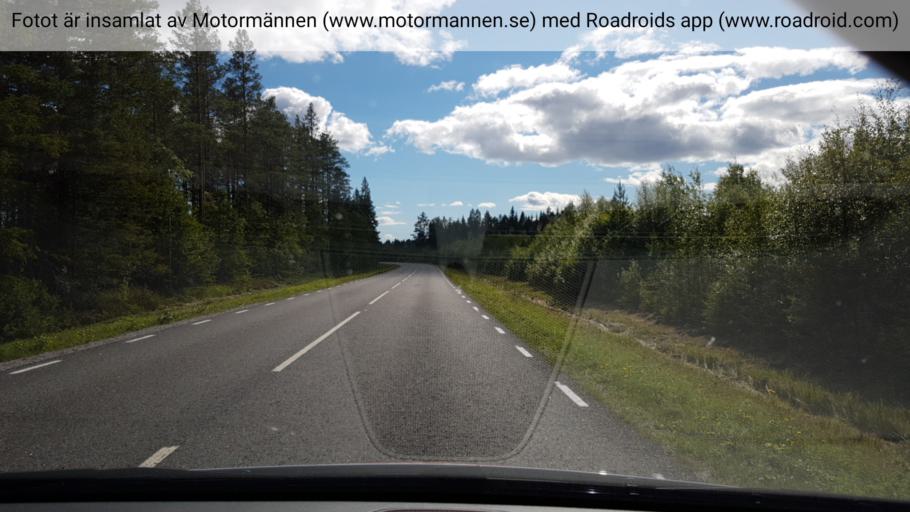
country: SE
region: Vaesterbotten
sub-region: Umea Kommun
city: Hoernefors
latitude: 63.6598
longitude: 19.9260
